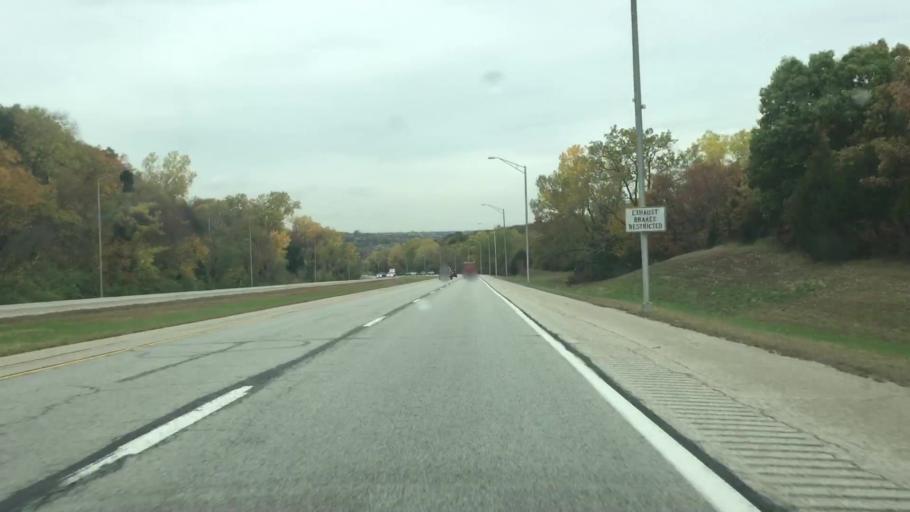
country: US
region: Kansas
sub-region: Wyandotte County
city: Edwardsville
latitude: 39.0107
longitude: -94.7956
